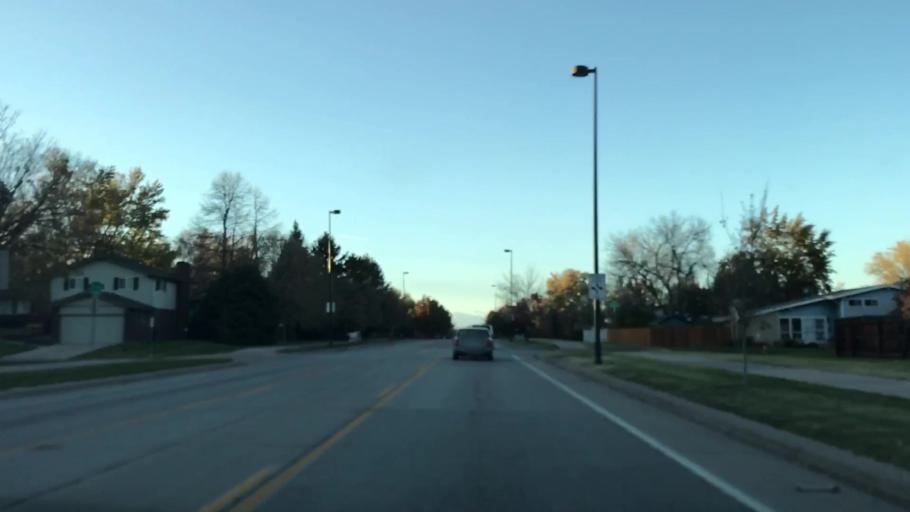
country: US
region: Colorado
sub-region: Arapahoe County
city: Glendale
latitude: 39.6631
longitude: -104.8886
